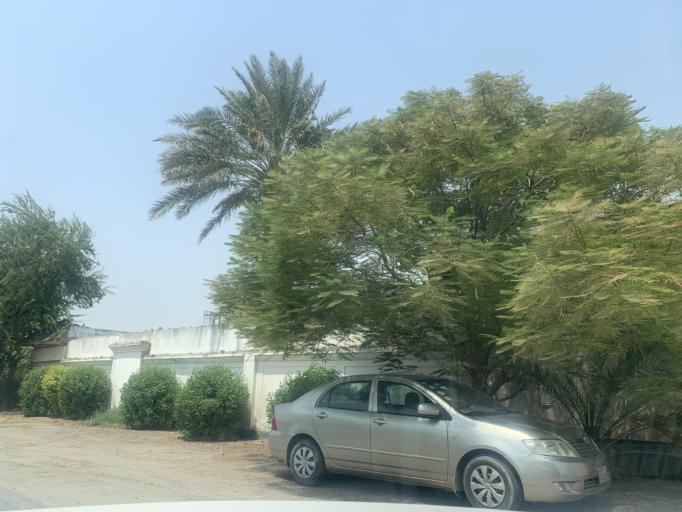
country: BH
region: Central Governorate
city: Madinat Hamad
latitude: 26.1250
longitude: 50.4718
